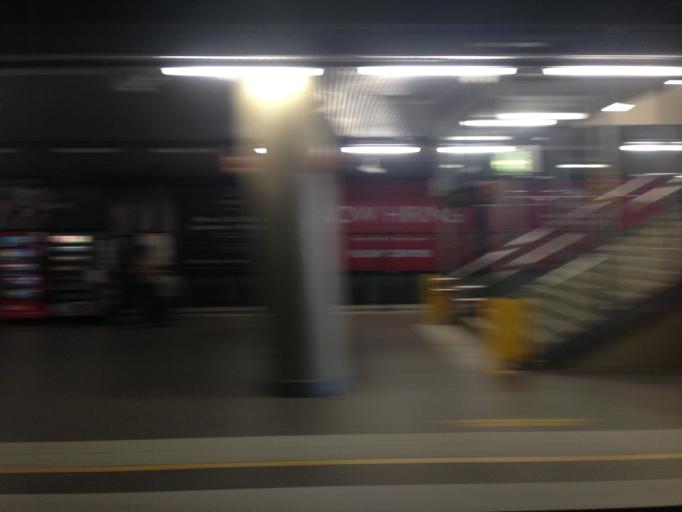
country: AU
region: New South Wales
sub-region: North Sydney
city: St Leonards
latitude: -33.8224
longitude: 151.1942
